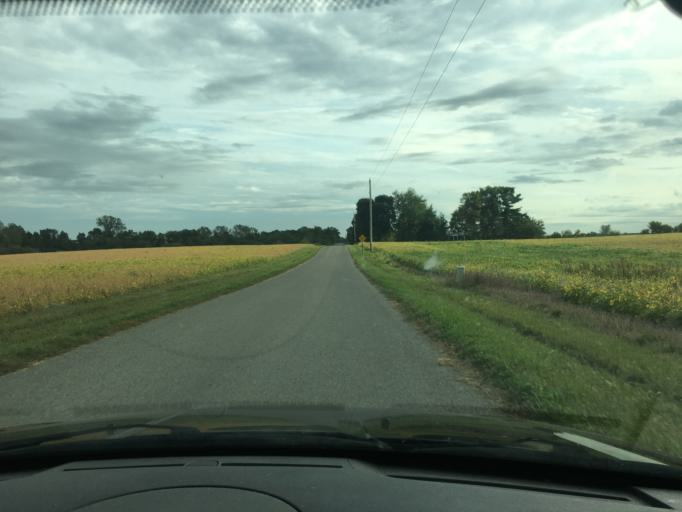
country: US
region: Ohio
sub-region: Logan County
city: Bellefontaine
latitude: 40.3190
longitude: -83.8064
